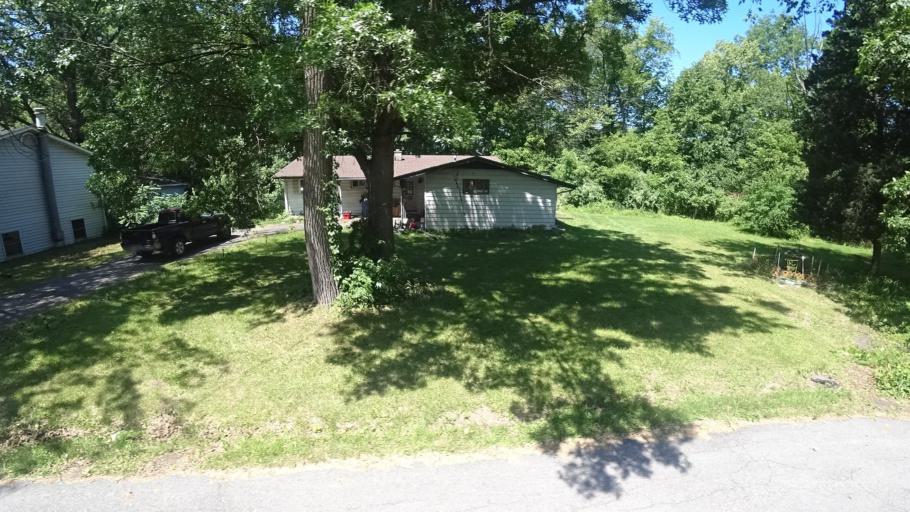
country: US
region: Indiana
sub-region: Porter County
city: Burns Harbor
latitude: 41.6152
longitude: -87.1269
